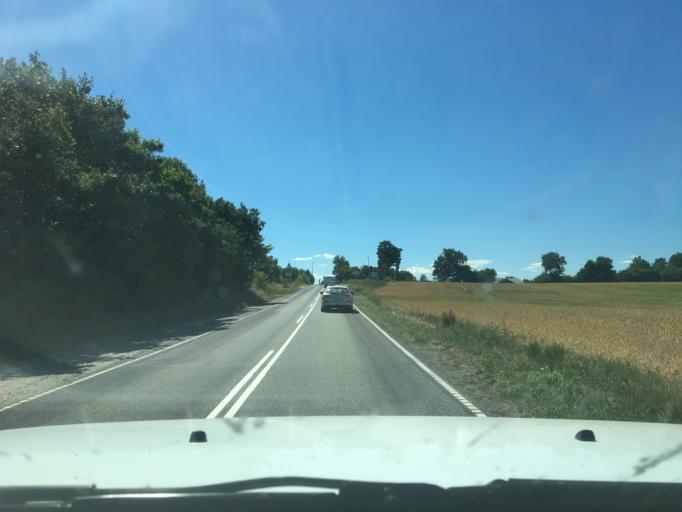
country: DK
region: Central Jutland
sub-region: Syddjurs Kommune
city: Hornslet
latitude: 56.3240
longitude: 10.3261
